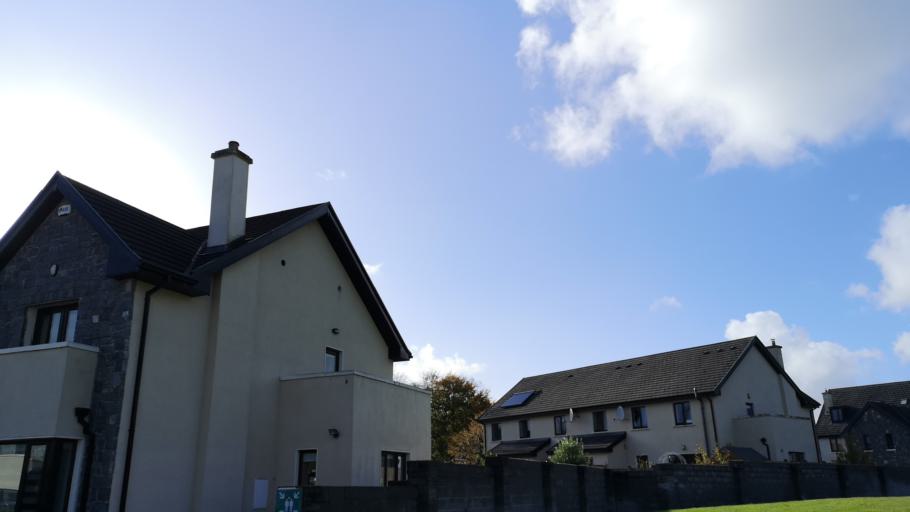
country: IE
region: Connaught
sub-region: County Galway
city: Athenry
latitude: 53.3016
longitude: -8.7613
